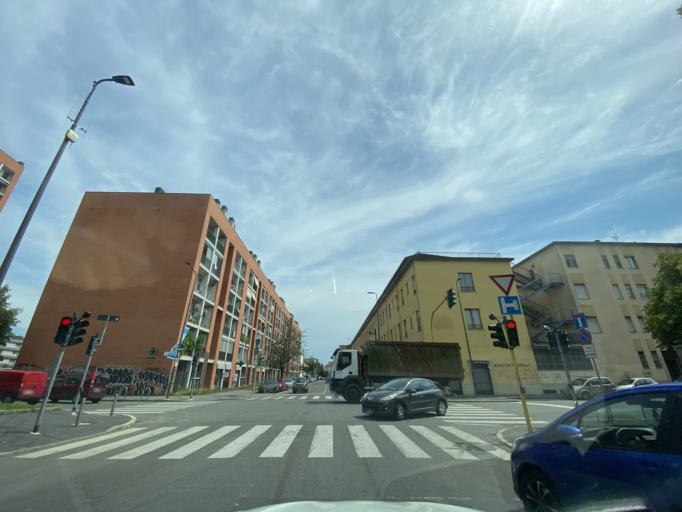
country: IT
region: Lombardy
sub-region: Citta metropolitana di Milano
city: Baranzate
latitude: 45.5164
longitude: 9.1276
